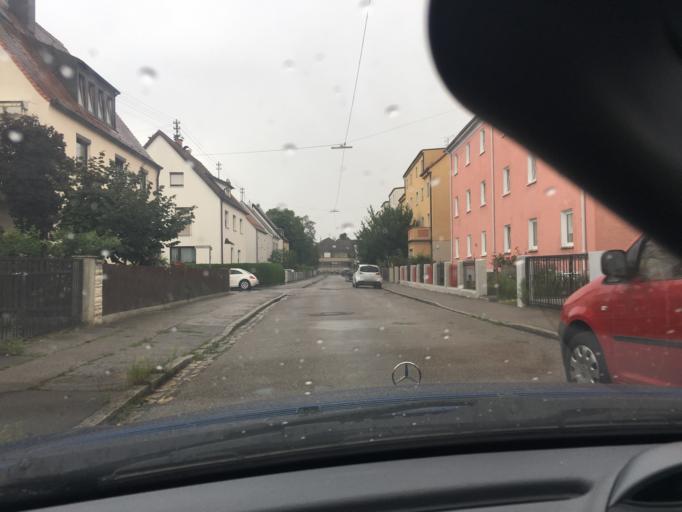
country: DE
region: Bavaria
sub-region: Swabia
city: Stadtbergen
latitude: 48.3829
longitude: 10.8641
